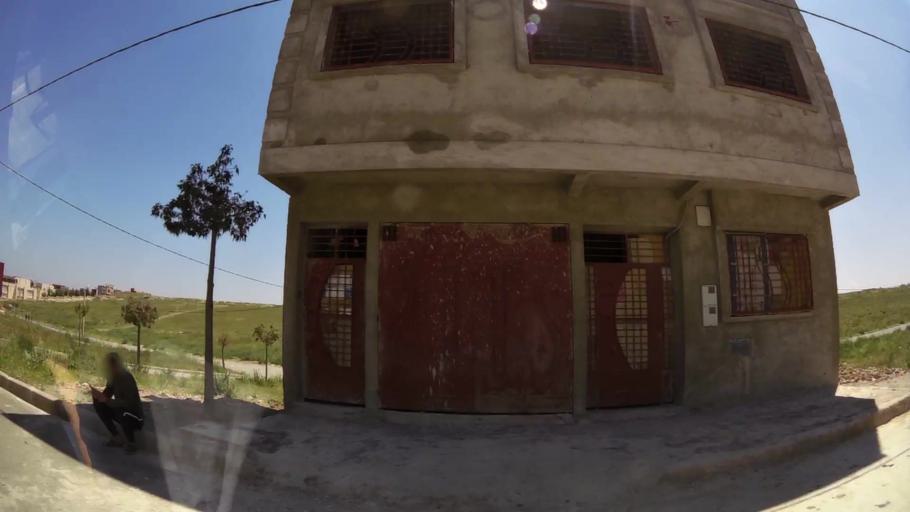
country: MA
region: Oriental
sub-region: Oujda-Angad
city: Oujda
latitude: 34.6769
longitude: -1.9514
